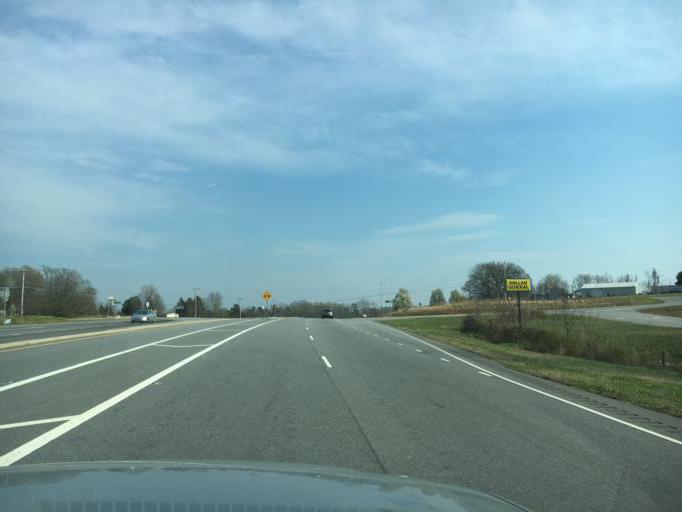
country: US
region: North Carolina
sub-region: Rutherford County
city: Forest City
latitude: 35.2375
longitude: -81.8501
